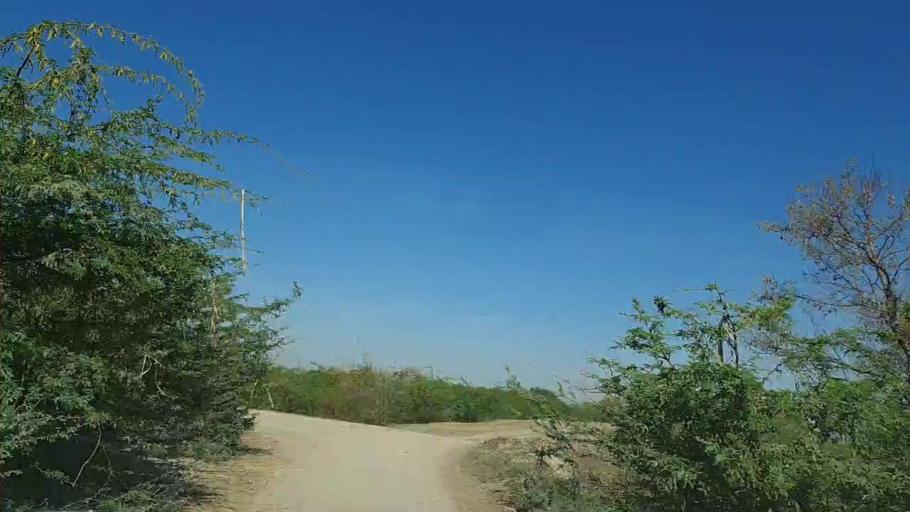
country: PK
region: Sindh
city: Dhoro Naro
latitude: 25.5161
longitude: 69.5287
